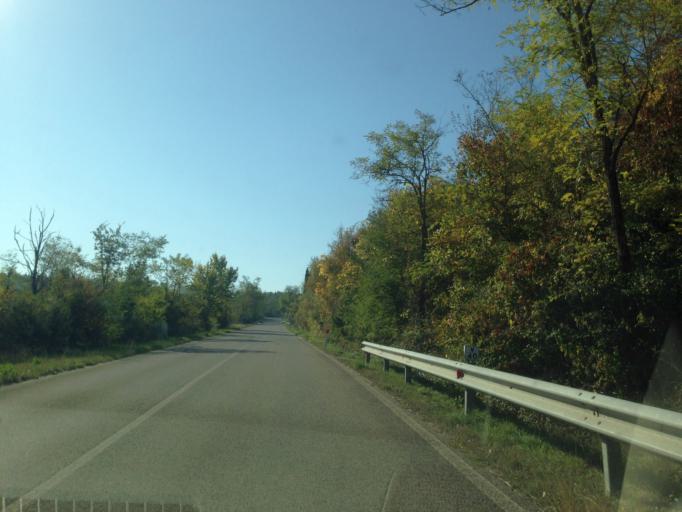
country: IT
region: Tuscany
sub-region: Provincia di Siena
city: Castellina in Chianti
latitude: 43.4823
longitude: 11.2979
